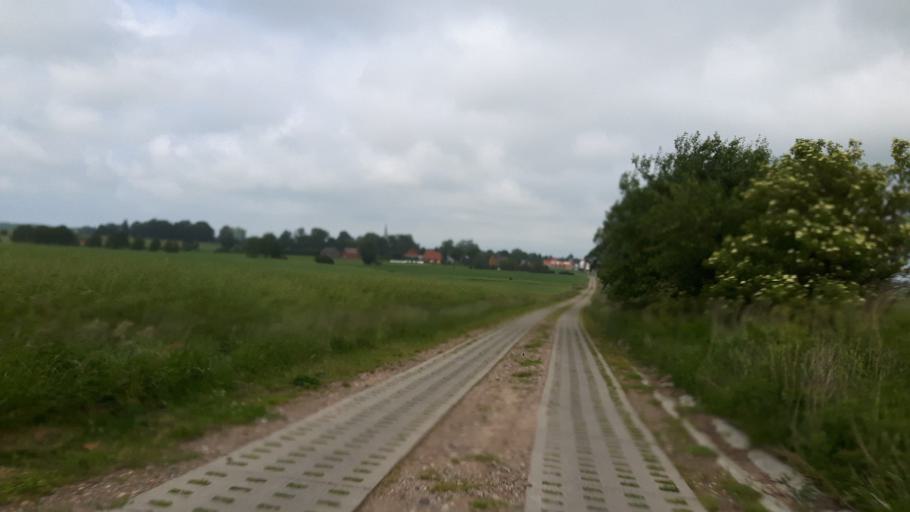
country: PL
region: West Pomeranian Voivodeship
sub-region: Powiat koszalinski
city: Sianow
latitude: 54.2894
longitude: 16.2657
